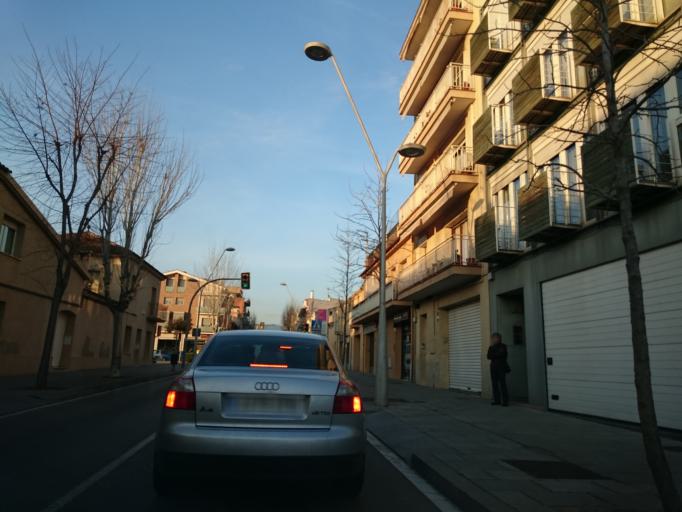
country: ES
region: Catalonia
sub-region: Provincia de Barcelona
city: Les Franqueses del Valles
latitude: 41.6242
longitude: 2.2937
